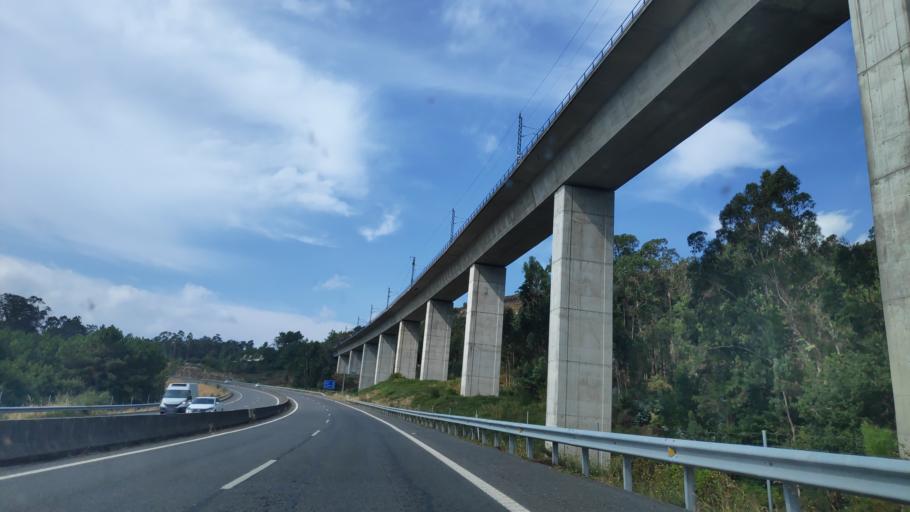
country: ES
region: Galicia
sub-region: Provincia da Coruna
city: Rois
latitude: 42.7265
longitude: -8.7189
